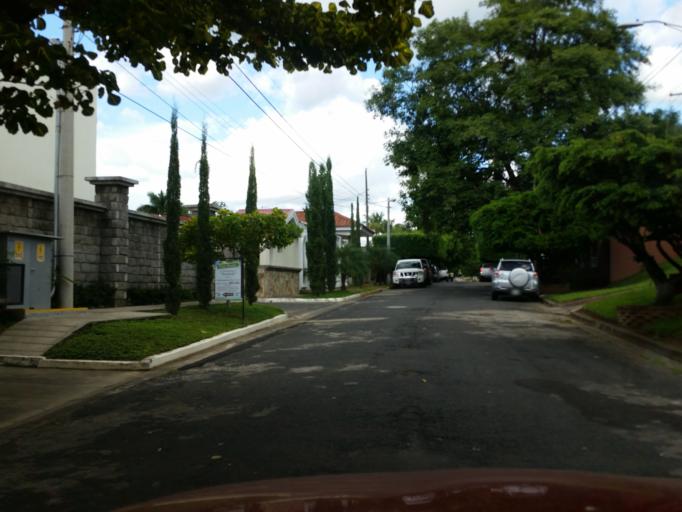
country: NI
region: Managua
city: Managua
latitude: 12.1023
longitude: -86.2692
